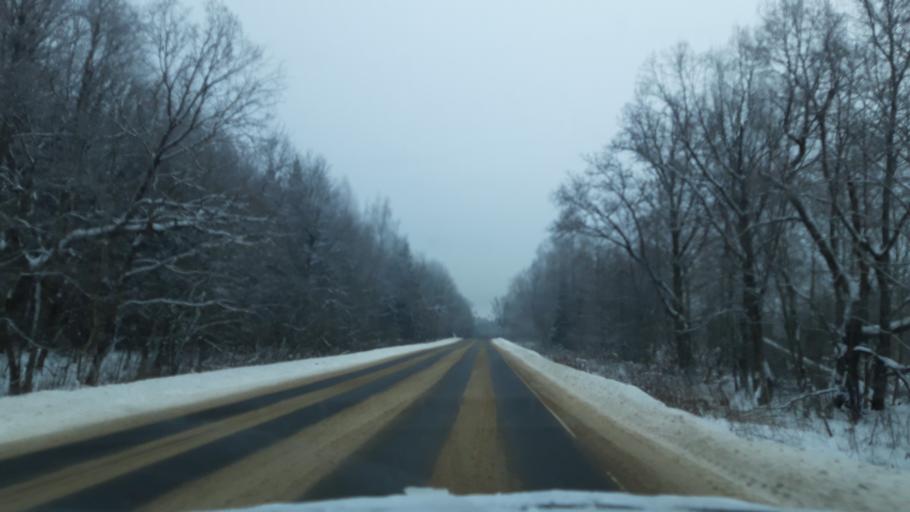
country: RU
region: Moskovskaya
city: Avtopoligon
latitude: 56.2771
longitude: 37.3700
